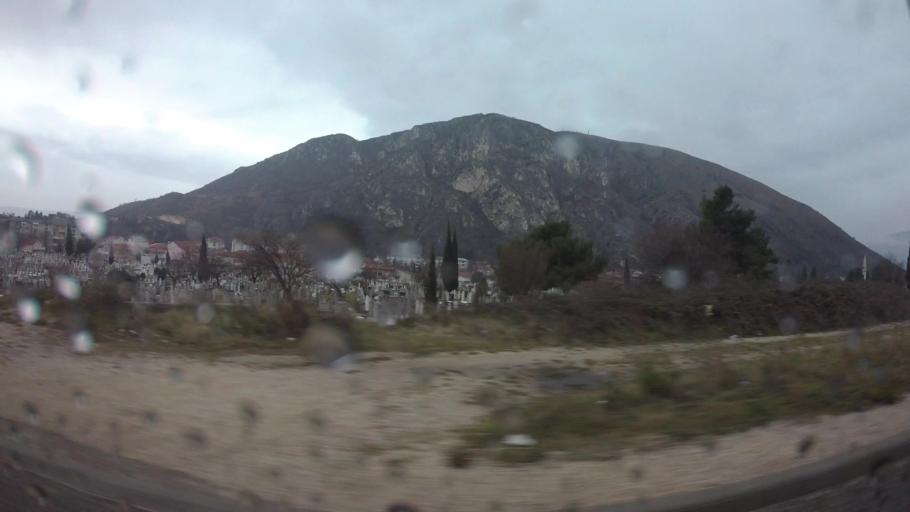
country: BA
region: Federation of Bosnia and Herzegovina
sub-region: Hercegovacko-Bosanski Kanton
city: Mostar
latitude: 43.3305
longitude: 17.8213
